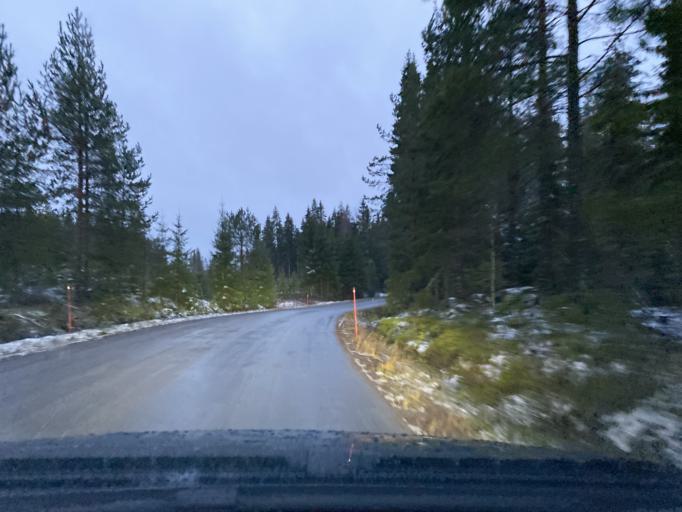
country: FI
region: Pirkanmaa
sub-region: Lounais-Pirkanmaa
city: Punkalaidun
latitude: 61.1484
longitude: 22.9671
